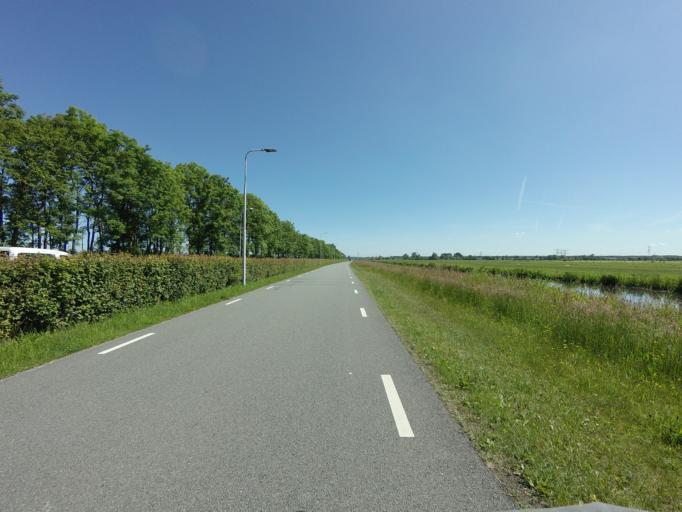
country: NL
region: Utrecht
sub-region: Stichtse Vecht
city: Breukelen
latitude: 52.1594
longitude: 4.9641
